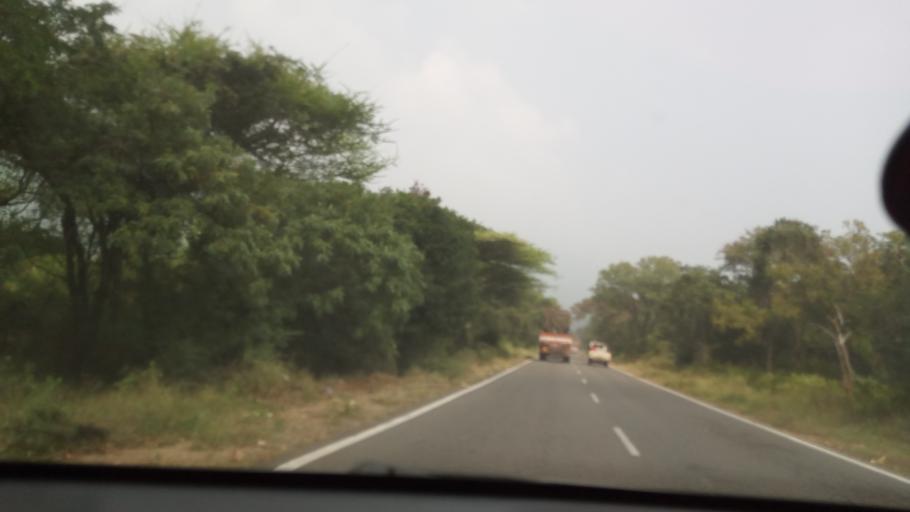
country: IN
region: Tamil Nadu
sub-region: Erode
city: Sathyamangalam
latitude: 11.5732
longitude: 77.1340
